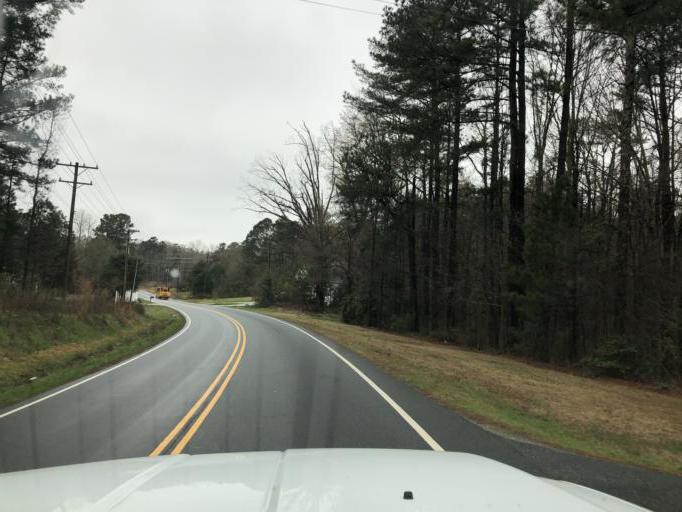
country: US
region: North Carolina
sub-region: Mecklenburg County
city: Huntersville
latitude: 35.3448
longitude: -80.9050
